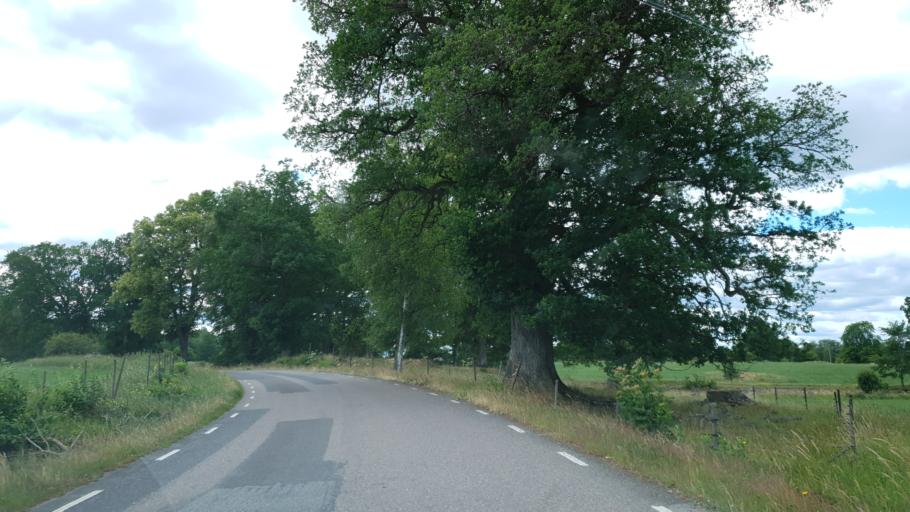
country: SE
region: Kalmar
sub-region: Hultsfreds Kommun
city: Virserum
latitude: 57.0591
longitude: 15.5906
